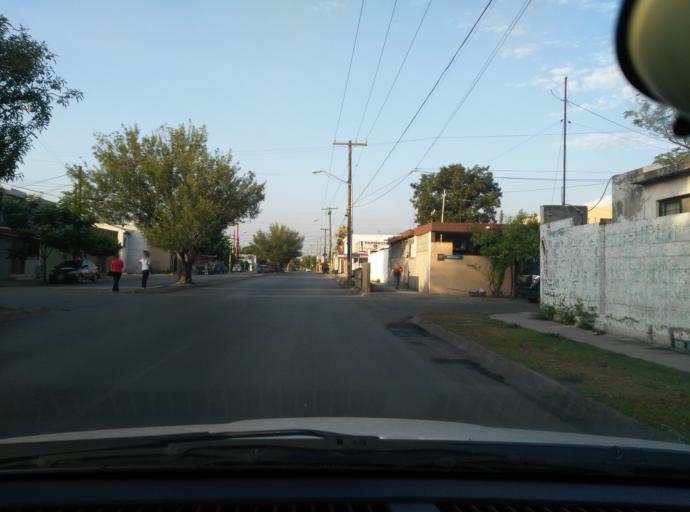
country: MX
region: Nuevo Leon
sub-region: San Nicolas de los Garza
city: San Nicolas de los Garza
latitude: 25.7655
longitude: -100.2495
